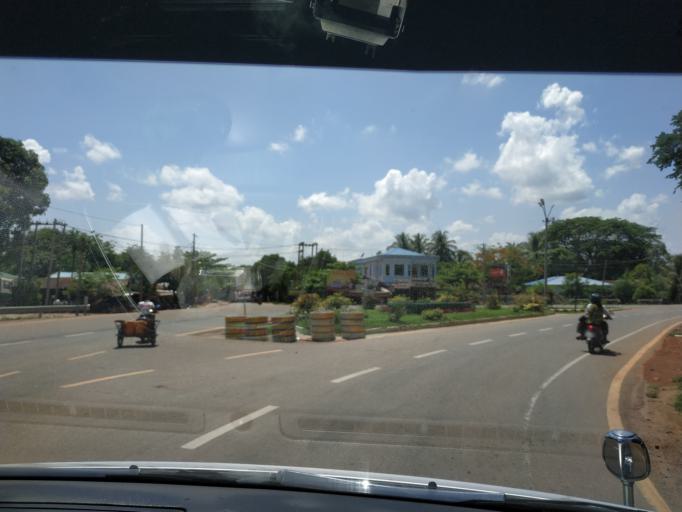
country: MM
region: Mon
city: Kyaikto
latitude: 17.3141
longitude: 97.0188
